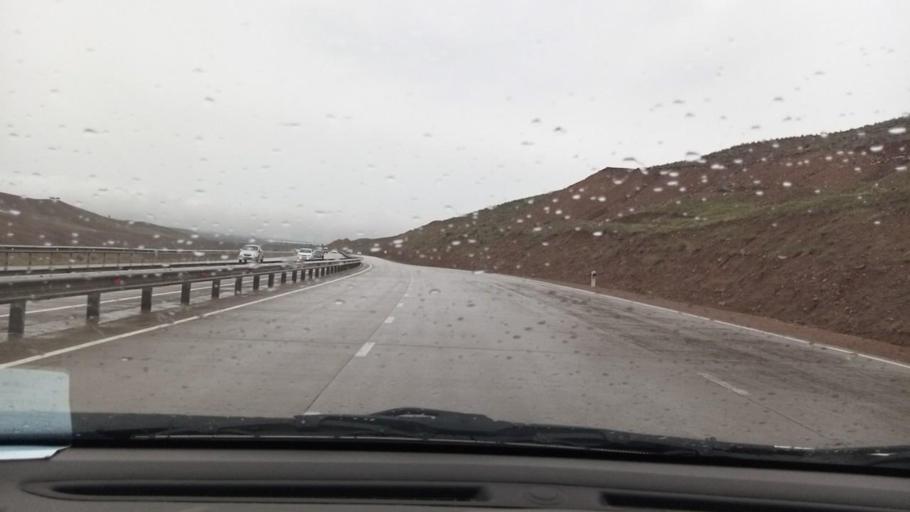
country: UZ
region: Namangan
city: Pop Shahri
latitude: 40.9312
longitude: 70.7034
